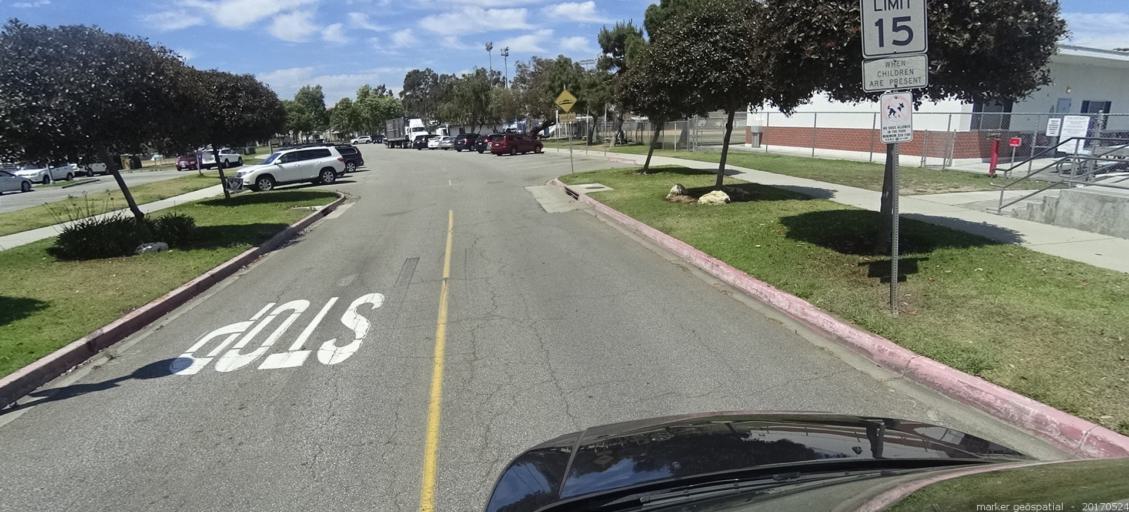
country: US
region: California
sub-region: Los Angeles County
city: Redondo Beach
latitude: 33.8293
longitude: -118.3791
